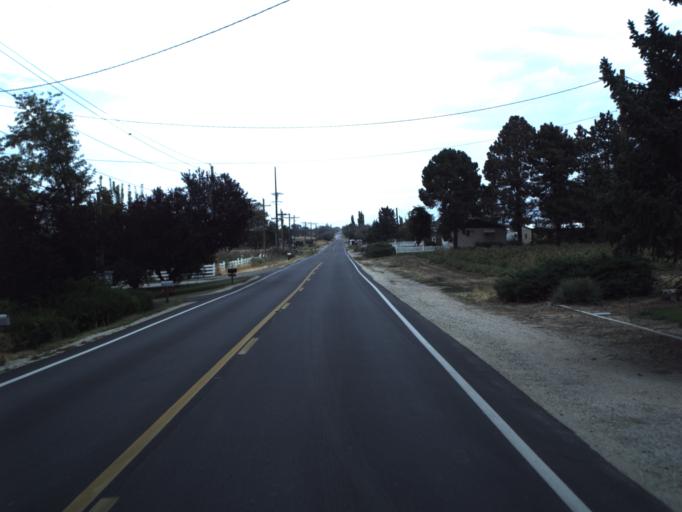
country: US
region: Utah
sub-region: Weber County
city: West Haven
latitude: 41.2110
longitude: -112.0929
